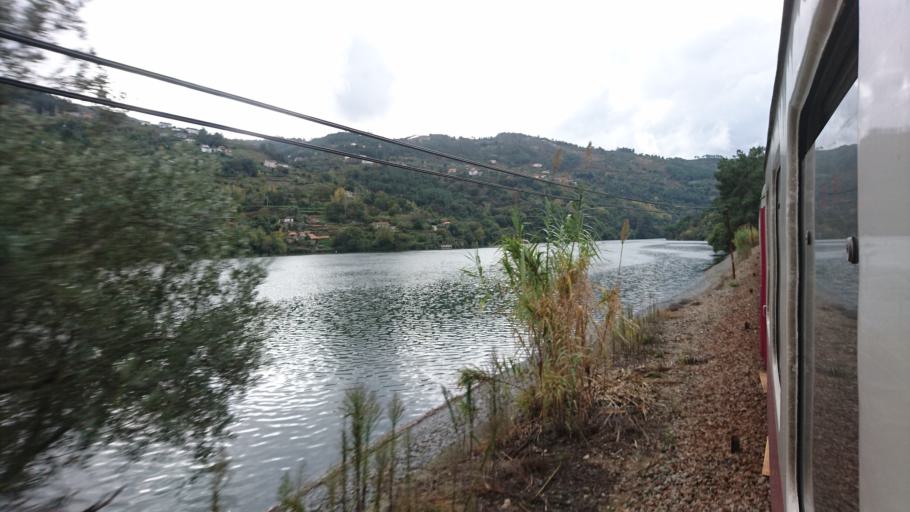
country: PT
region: Viseu
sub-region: Cinfaes
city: Cinfaes
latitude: 41.0957
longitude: -8.0400
